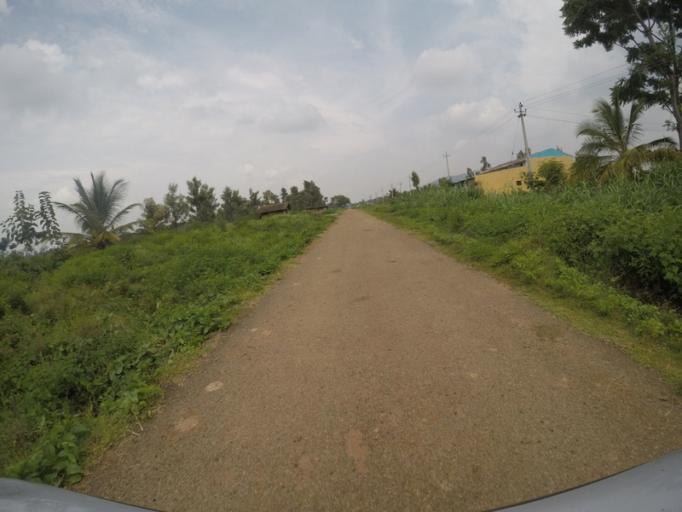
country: IN
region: Karnataka
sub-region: Mandya
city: Malavalli
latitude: 12.4134
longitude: 77.2114
